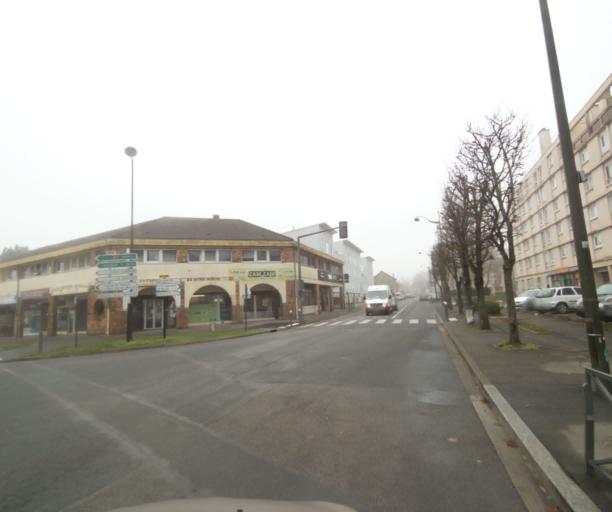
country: FR
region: Ile-de-France
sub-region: Departement de Seine-Saint-Denis
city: Clichy-sous-Bois
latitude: 48.9114
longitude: 2.5496
